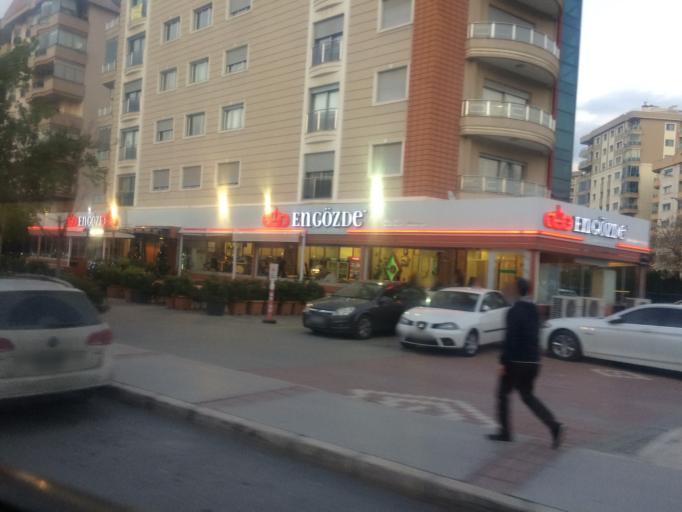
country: TR
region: Izmir
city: Karsiyaka
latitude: 38.4635
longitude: 27.0960
